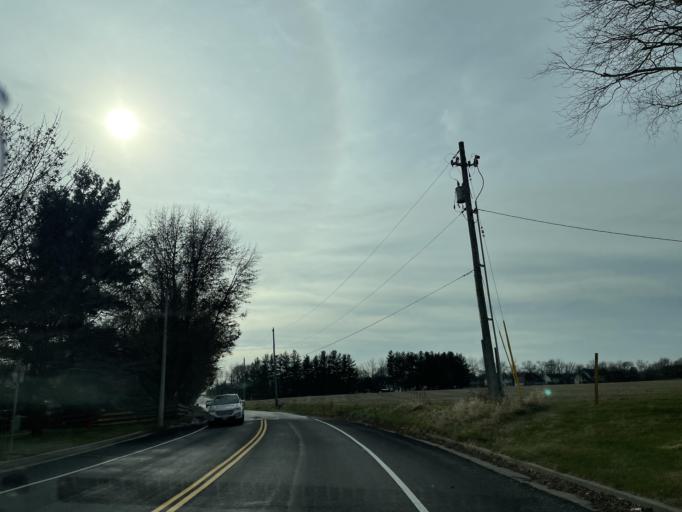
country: US
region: Illinois
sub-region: Sangamon County
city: Leland Grove
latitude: 39.7810
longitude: -89.7346
